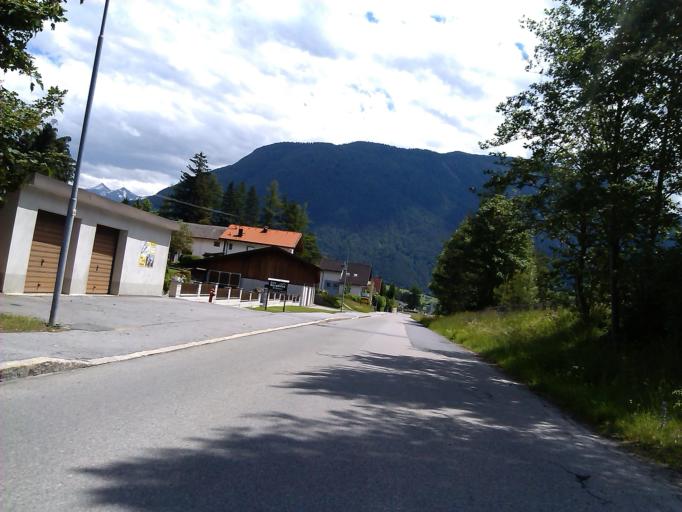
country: AT
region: Tyrol
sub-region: Politischer Bezirk Imst
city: Nassereith
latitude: 47.3202
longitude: 10.8294
